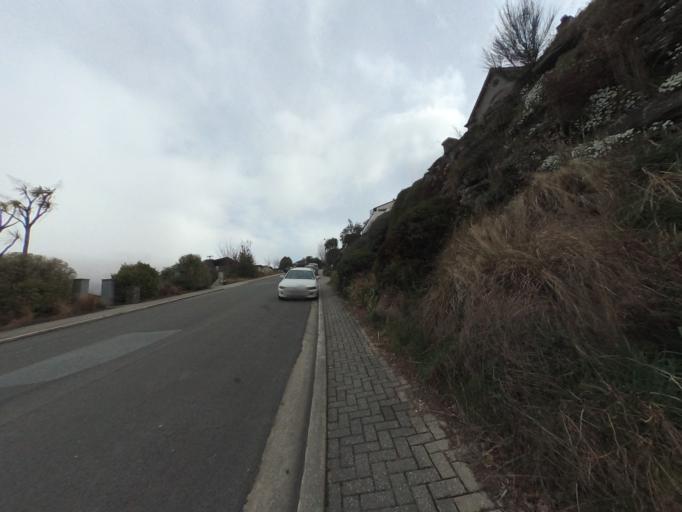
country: NZ
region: Otago
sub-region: Queenstown-Lakes District
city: Queenstown
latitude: -45.0395
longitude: 168.6367
